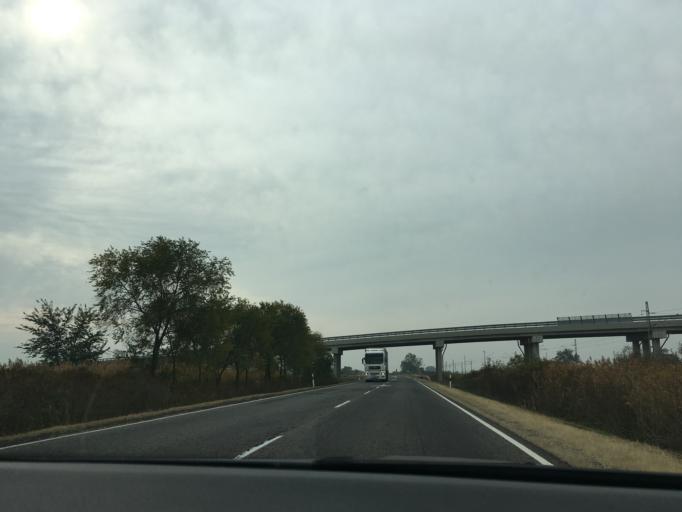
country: HU
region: Jasz-Nagykun-Szolnok
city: Karcag
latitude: 47.2628
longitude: 20.8527
